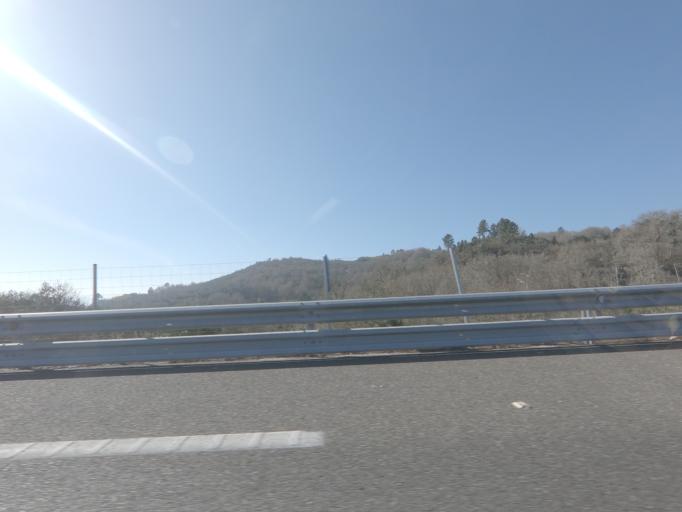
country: ES
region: Galicia
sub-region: Provincia de Ourense
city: Punxin
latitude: 42.3910
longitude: -7.9966
